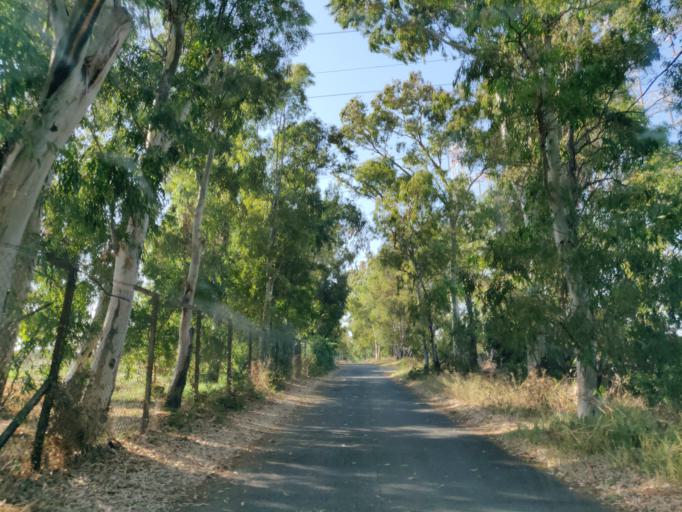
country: IT
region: Latium
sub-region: Citta metropolitana di Roma Capitale
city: Aurelia
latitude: 42.1312
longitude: 11.7659
